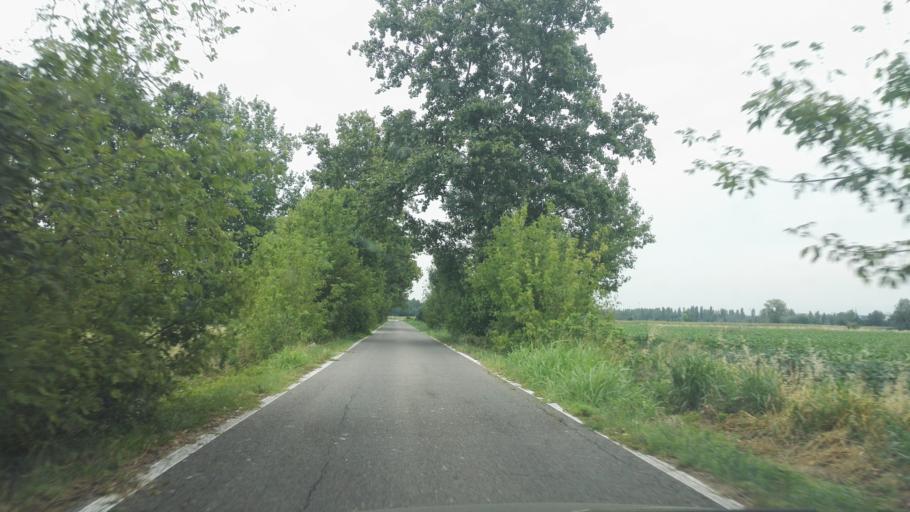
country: IT
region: Lombardy
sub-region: Citta metropolitana di Milano
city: Mezzate
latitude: 45.4557
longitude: 9.2959
